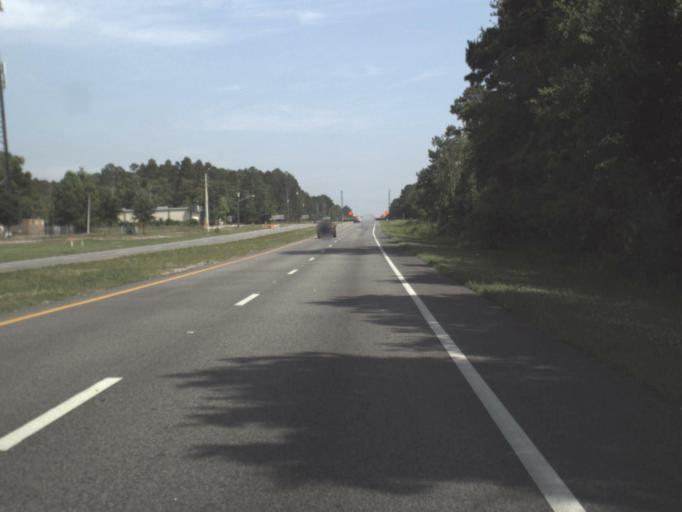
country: US
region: Florida
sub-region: Saint Johns County
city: Palm Valley
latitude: 30.0974
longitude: -81.4716
